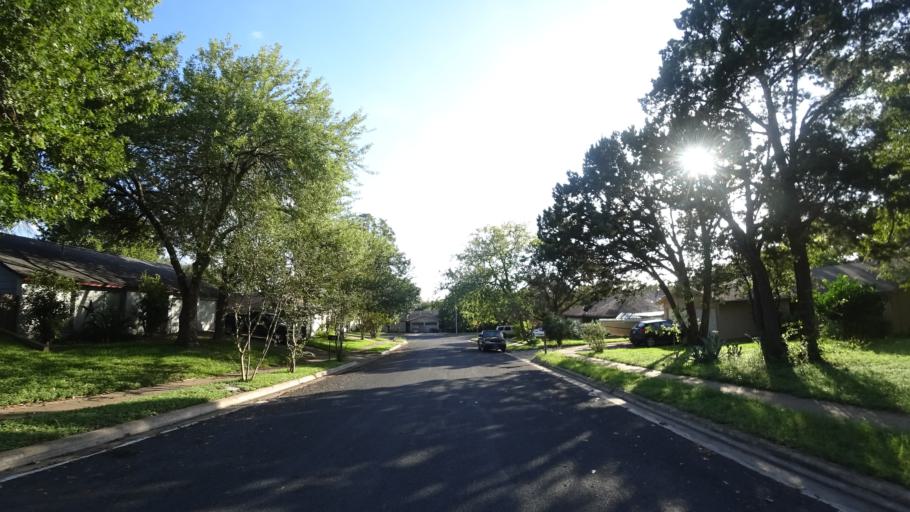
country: US
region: Texas
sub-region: Travis County
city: Onion Creek
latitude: 30.1960
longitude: -97.7961
